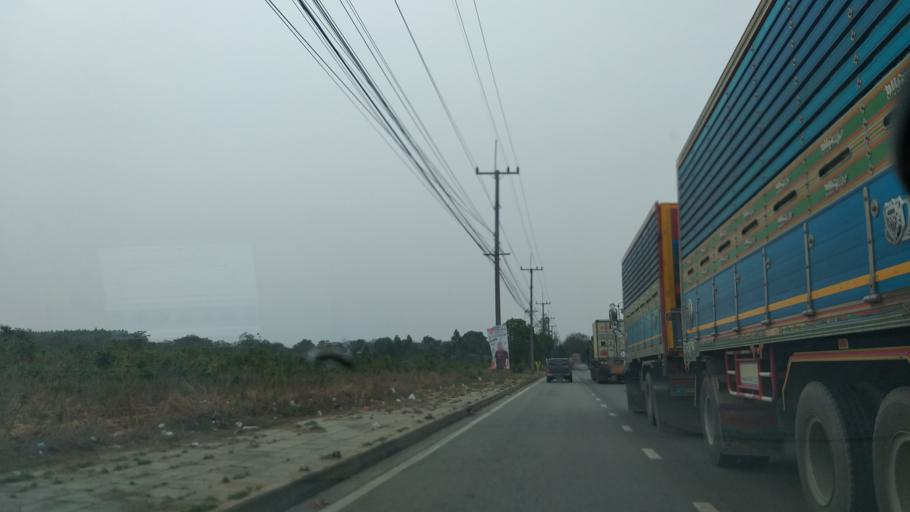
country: TH
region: Chon Buri
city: Ko Chan
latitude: 13.4892
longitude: 101.2761
